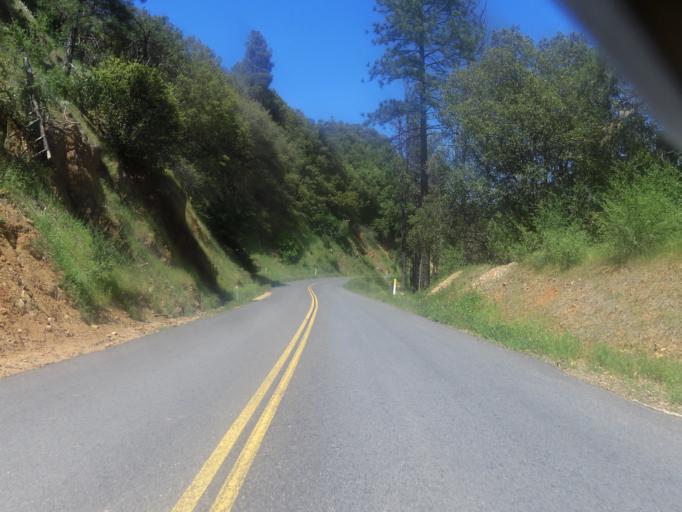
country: US
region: California
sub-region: Mariposa County
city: Midpines
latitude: 37.5129
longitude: -119.8475
